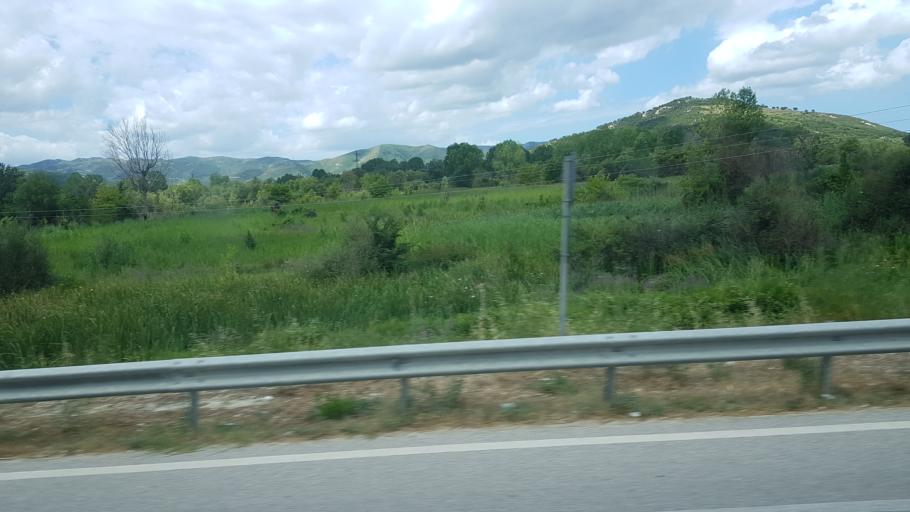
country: AL
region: Fier
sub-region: Rrethi i Mallakastres
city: Hekal
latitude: 40.5164
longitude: 19.7421
